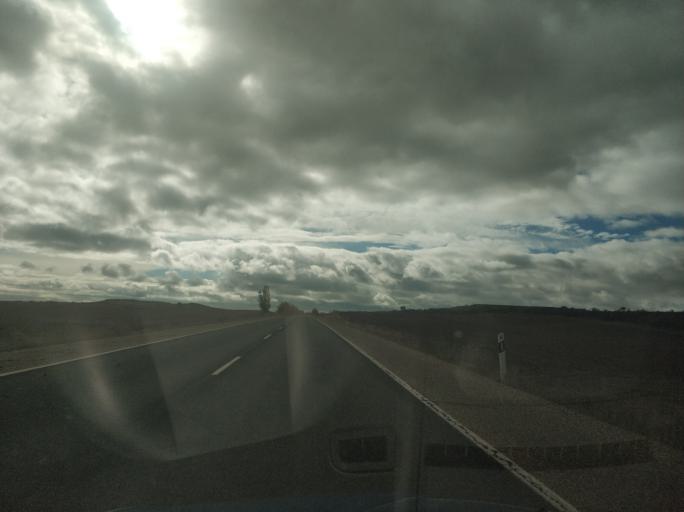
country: ES
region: Castille and Leon
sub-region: Provincia de Zamora
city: Castrillo de la Guarena
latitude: 41.2168
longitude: -5.3185
